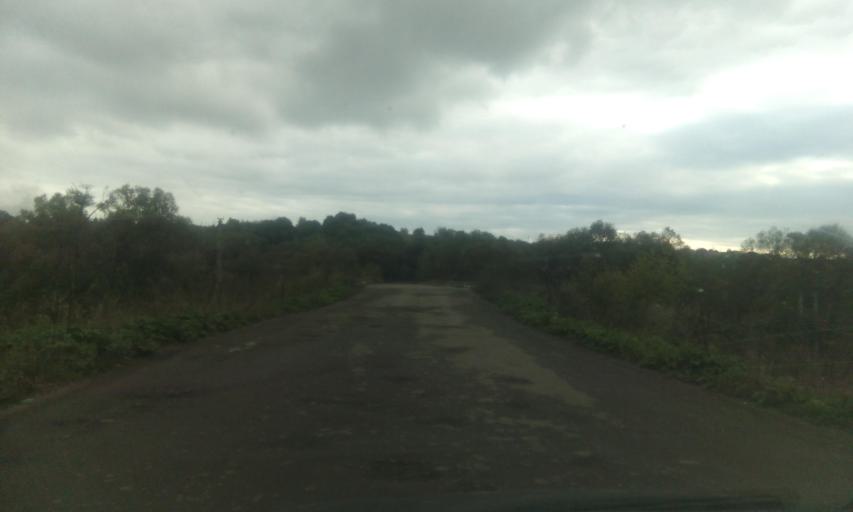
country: RU
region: Tula
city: Gritsovskiy
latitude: 54.1201
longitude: 38.1692
